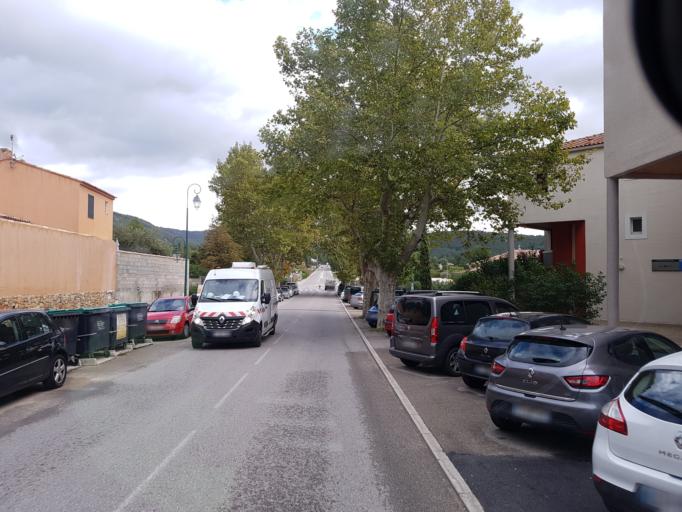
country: FR
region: Provence-Alpes-Cote d'Azur
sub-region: Departement des Bouches-du-Rhone
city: Cuges-les-Pins
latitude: 43.2758
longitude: 5.7042
